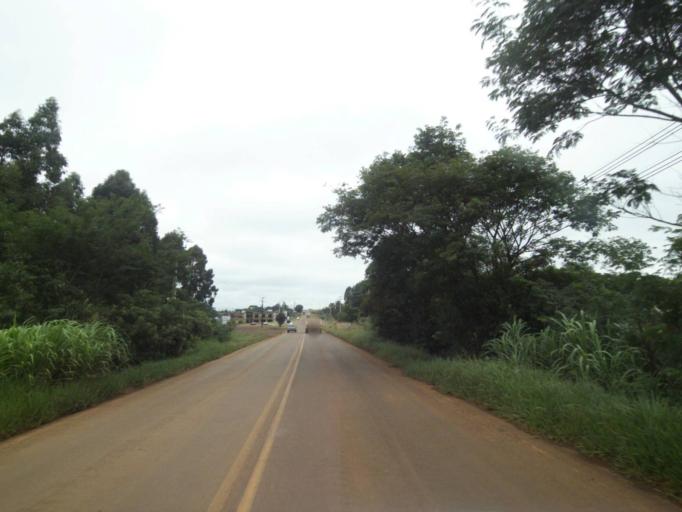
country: BR
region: Parana
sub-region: Pitanga
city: Pitanga
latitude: -24.9266
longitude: -51.8737
